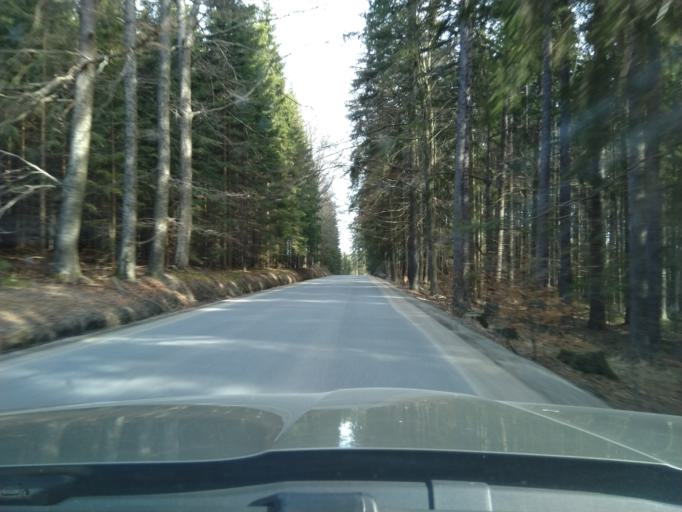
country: CZ
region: Jihocesky
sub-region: Okres Prachatice
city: Stachy
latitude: 49.0611
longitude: 13.6560
